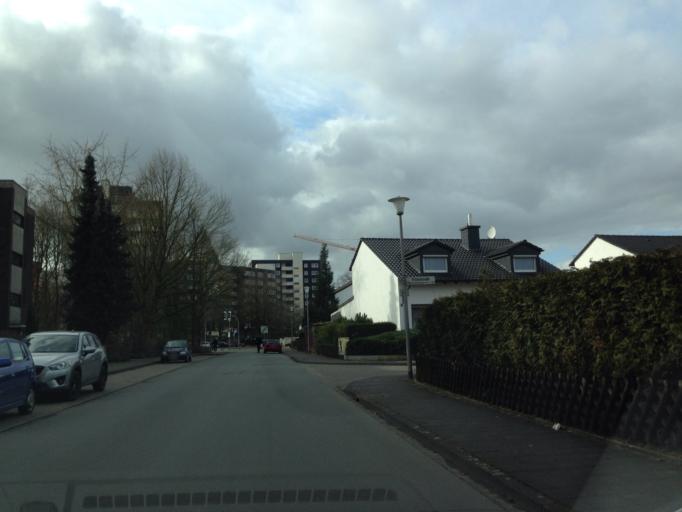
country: DE
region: North Rhine-Westphalia
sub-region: Regierungsbezirk Munster
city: Muenster
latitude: 51.9985
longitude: 7.5992
